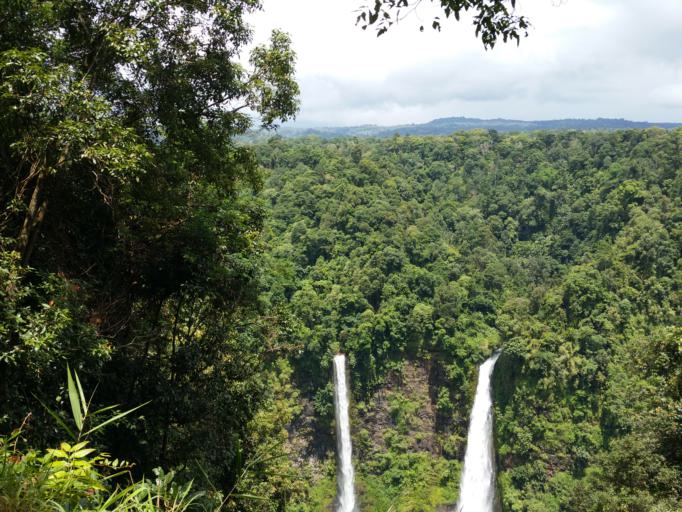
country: LA
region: Champasak
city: Pakxong
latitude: 15.1824
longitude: 106.1267
